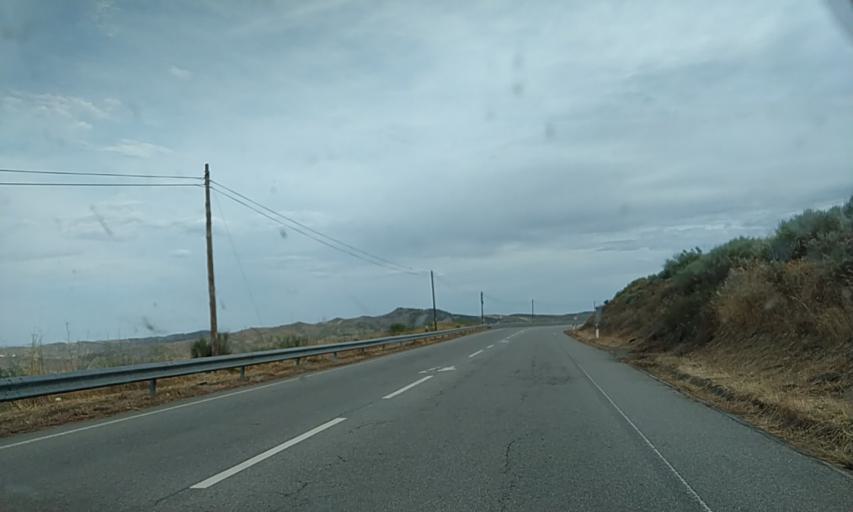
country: PT
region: Viseu
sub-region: Sao Joao da Pesqueira
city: Sao Joao da Pesqueira
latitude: 41.1183
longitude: -7.3888
